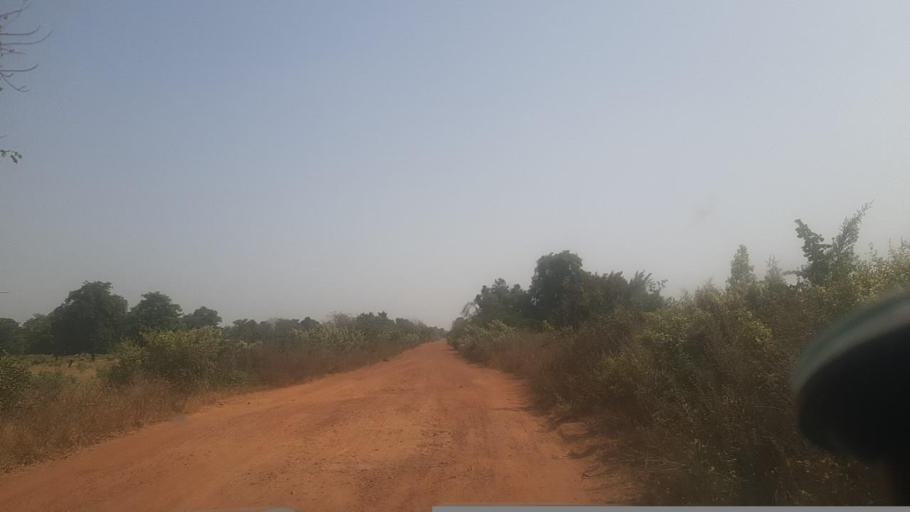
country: ML
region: Segou
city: Bla
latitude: 12.9202
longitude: -6.2581
